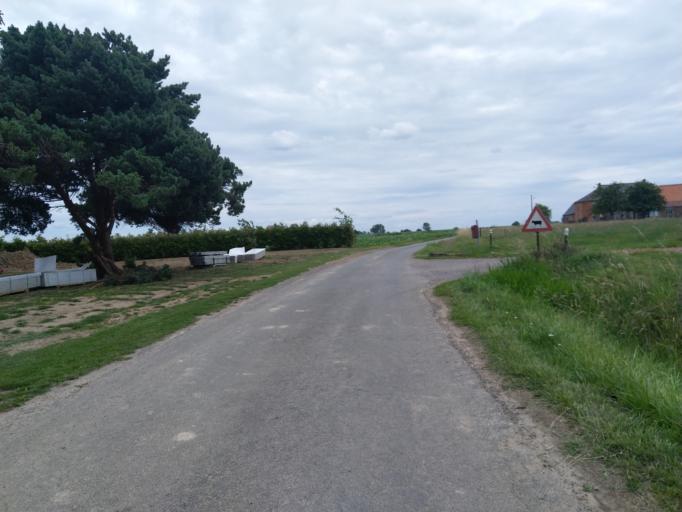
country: BE
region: Wallonia
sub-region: Province du Hainaut
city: Chievres
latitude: 50.5418
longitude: 3.8140
